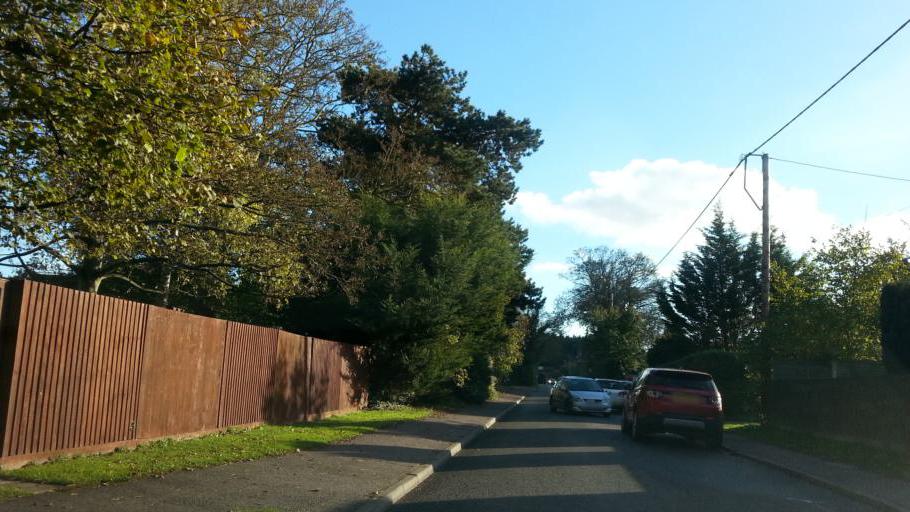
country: GB
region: England
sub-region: Suffolk
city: Thurston
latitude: 52.2525
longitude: 0.8062
